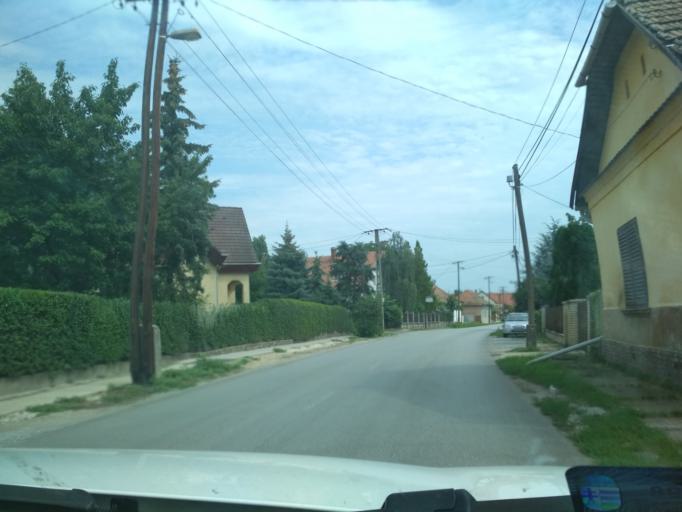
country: HU
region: Jasz-Nagykun-Szolnok
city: Tiszafured
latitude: 47.6137
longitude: 20.7558
